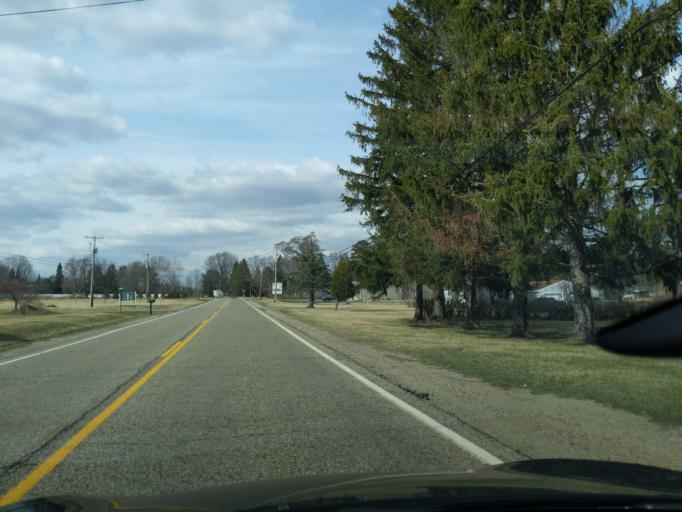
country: US
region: Michigan
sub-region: Jackson County
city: Jackson
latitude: 42.3401
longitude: -84.4135
